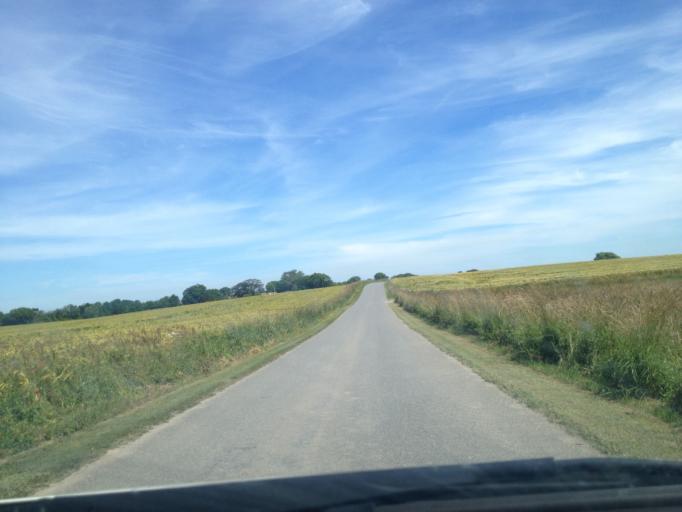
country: DK
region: Central Jutland
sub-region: Samso Kommune
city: Tranebjerg
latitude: 55.8731
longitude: 10.6689
